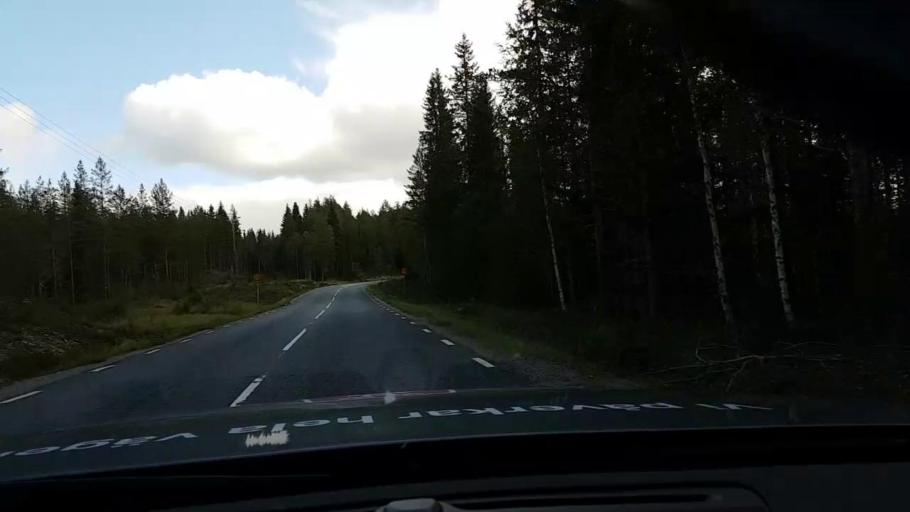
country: SE
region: Vaesterbotten
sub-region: Asele Kommun
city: Asele
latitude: 63.8078
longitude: 17.5373
